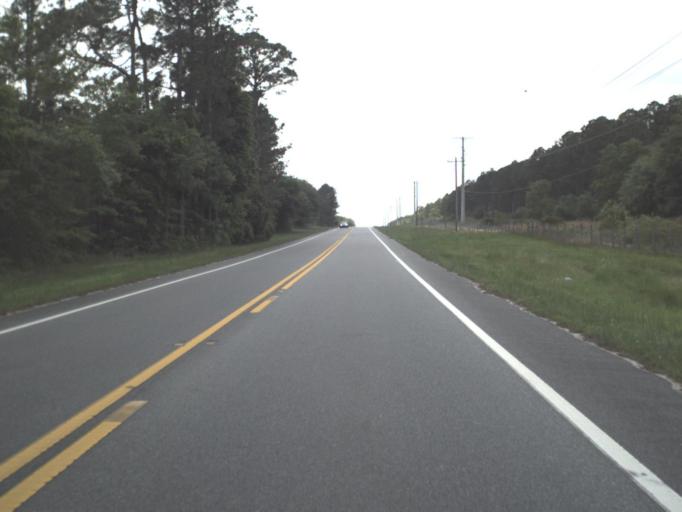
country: US
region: Florida
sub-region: Clay County
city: Keystone Heights
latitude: 29.8746
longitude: -81.9298
